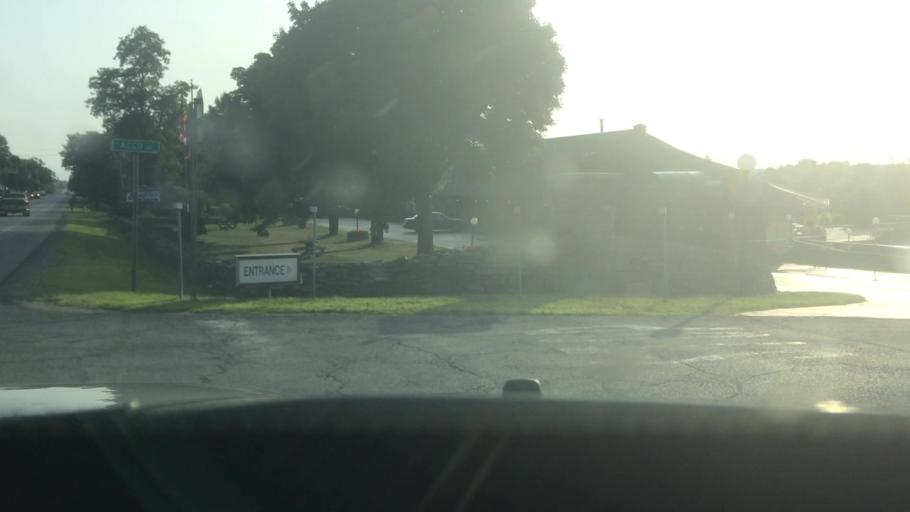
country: CA
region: Ontario
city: Prescott
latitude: 44.6741
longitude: -75.5273
